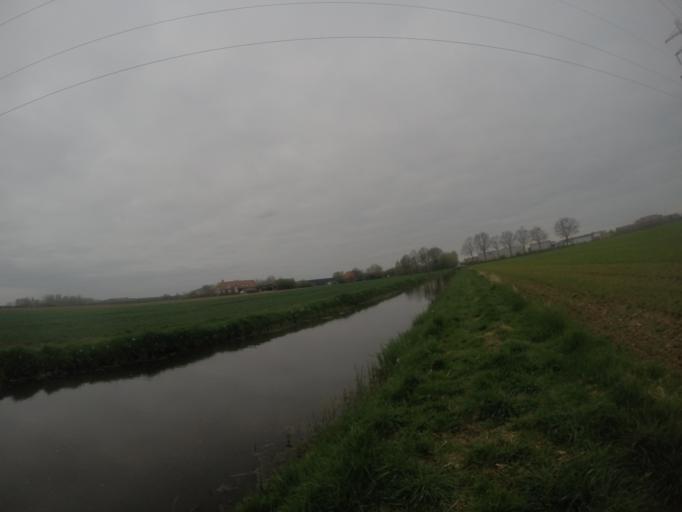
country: NL
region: Gelderland
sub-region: Gemeente Zutphen
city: Leesten
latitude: 52.1151
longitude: 6.2278
